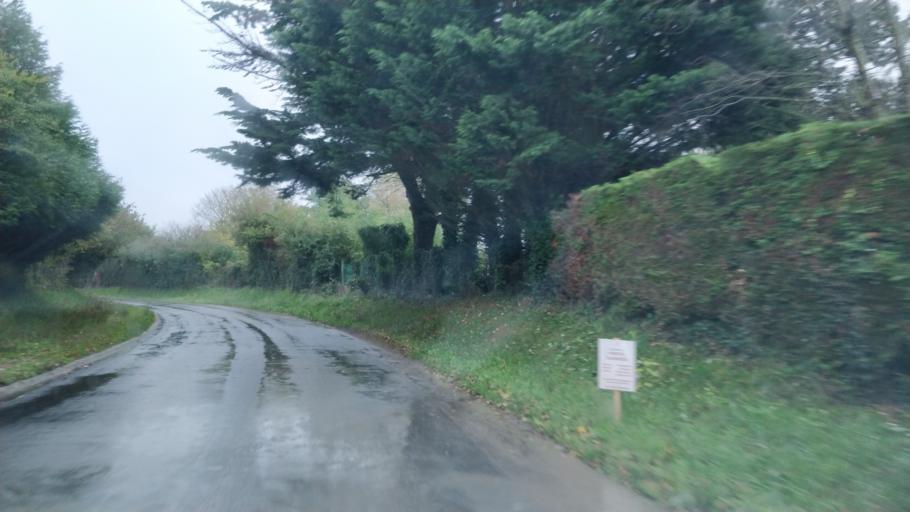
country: FR
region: Lower Normandy
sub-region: Departement de la Manche
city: Brehal
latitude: 48.9017
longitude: -1.5448
